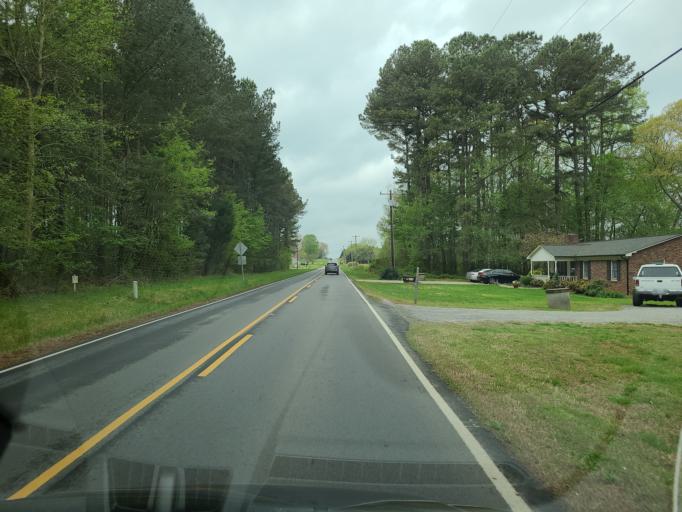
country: US
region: North Carolina
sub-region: Lincoln County
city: Lincolnton
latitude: 35.4570
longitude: -81.3026
